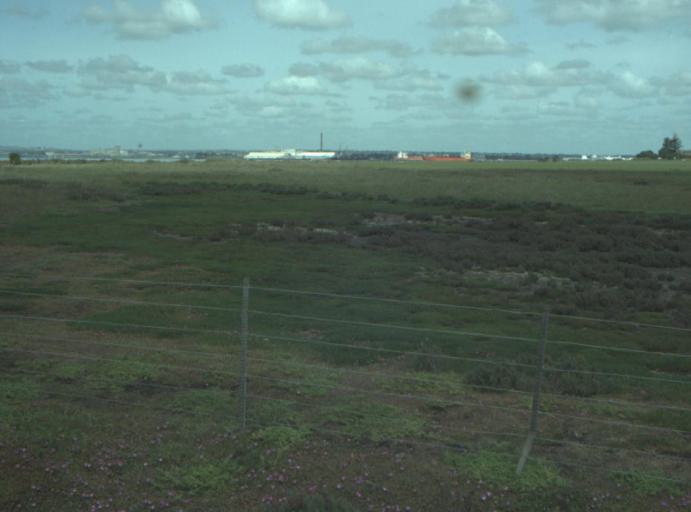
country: AU
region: Victoria
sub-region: Greater Geelong
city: Lara
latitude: -38.0838
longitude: 144.4224
